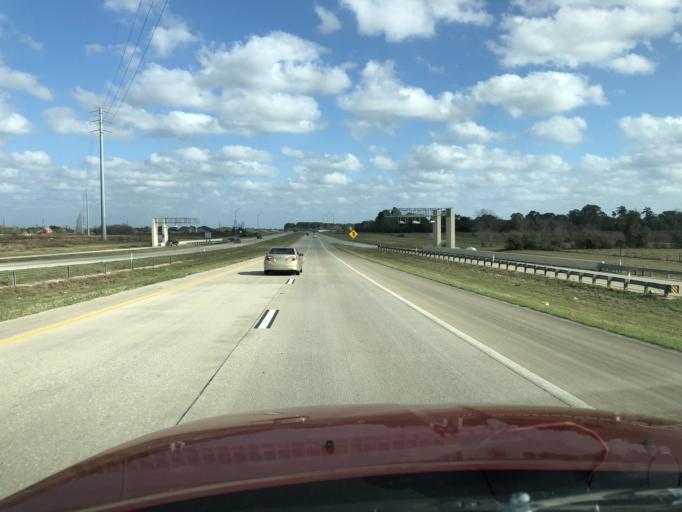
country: US
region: Texas
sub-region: Harris County
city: Cypress
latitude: 30.0534
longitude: -95.7321
